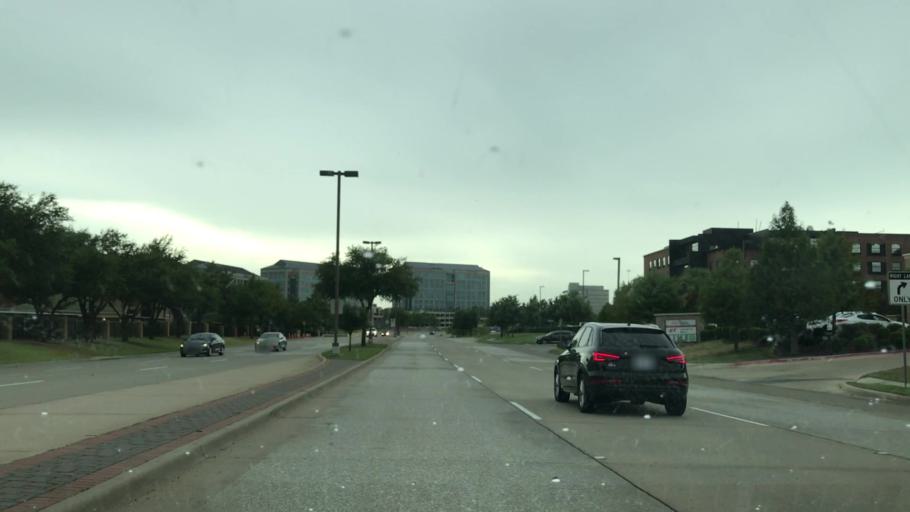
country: US
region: Texas
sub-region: Dallas County
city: Farmers Branch
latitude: 32.8959
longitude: -96.9614
